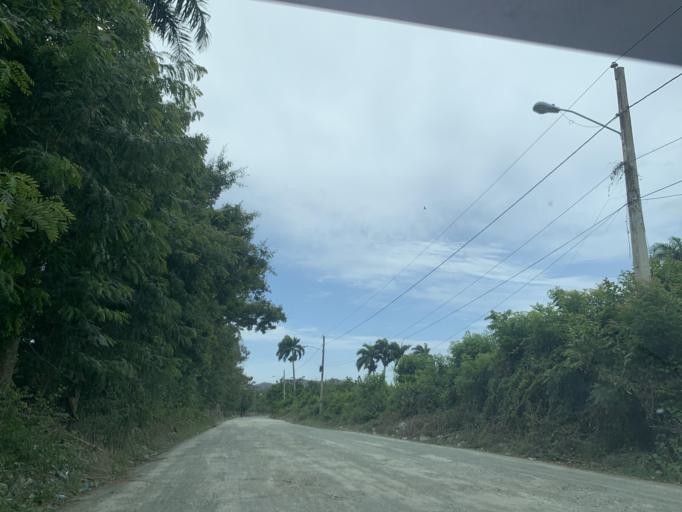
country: DO
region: Puerto Plata
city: Imbert
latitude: 19.8206
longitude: -70.7815
